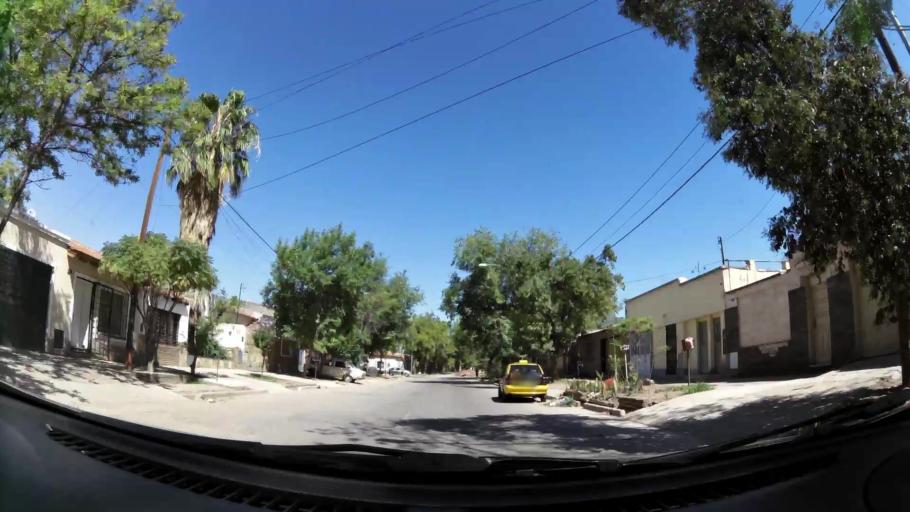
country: AR
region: Mendoza
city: Mendoza
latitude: -32.8792
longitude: -68.8209
